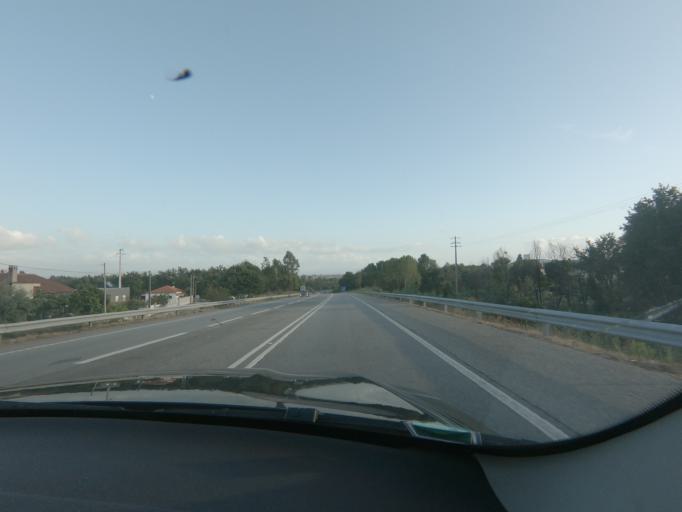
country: PT
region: Viseu
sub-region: Santa Comba Dao
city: Santa Comba Dao
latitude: 40.4180
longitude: -8.1223
